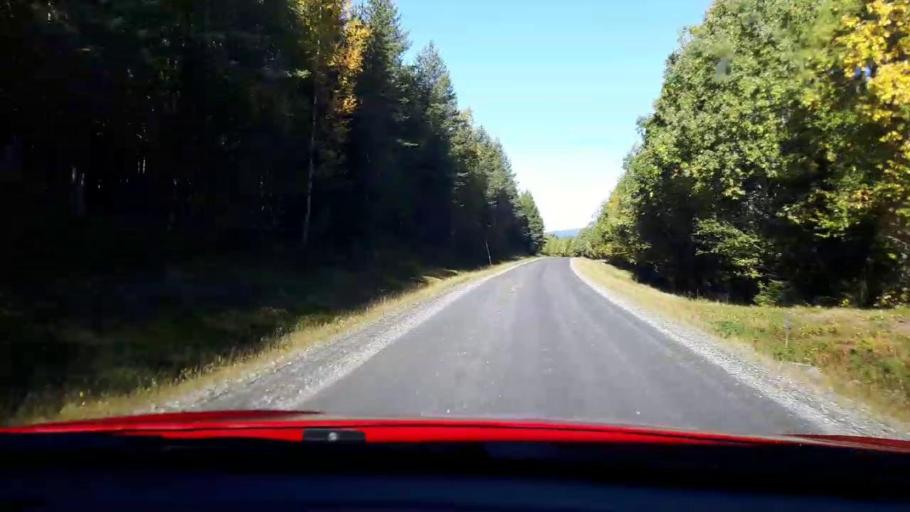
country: NO
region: Nord-Trondelag
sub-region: Lierne
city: Sandvika
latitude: 64.5378
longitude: 14.0100
